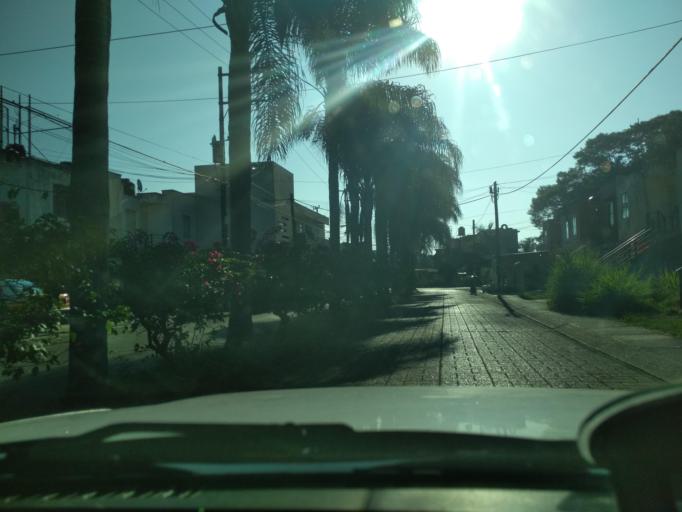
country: MX
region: Veracruz
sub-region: Fortin
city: Fraccionamiento Villas de la Llave
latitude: 18.9189
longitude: -96.9914
